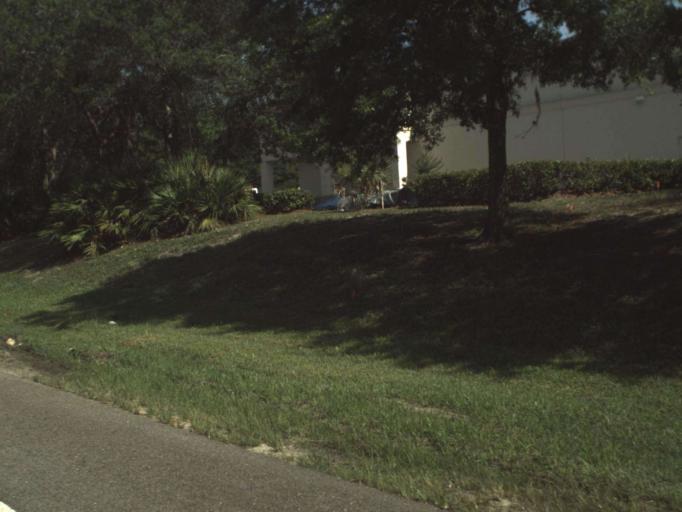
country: US
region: Florida
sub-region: Seminole County
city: Winter Springs
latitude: 28.7039
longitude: -81.2928
